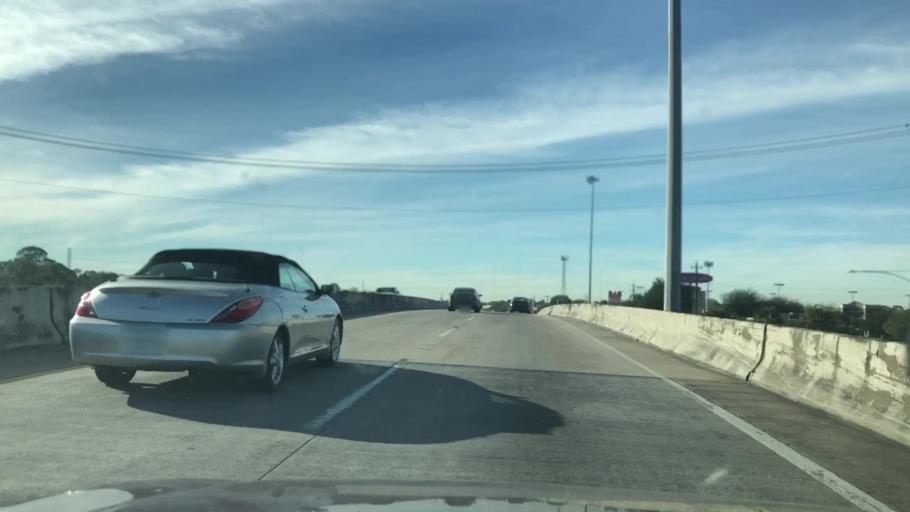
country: US
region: Texas
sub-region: Harris County
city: Bellaire
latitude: 29.6712
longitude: -95.4618
